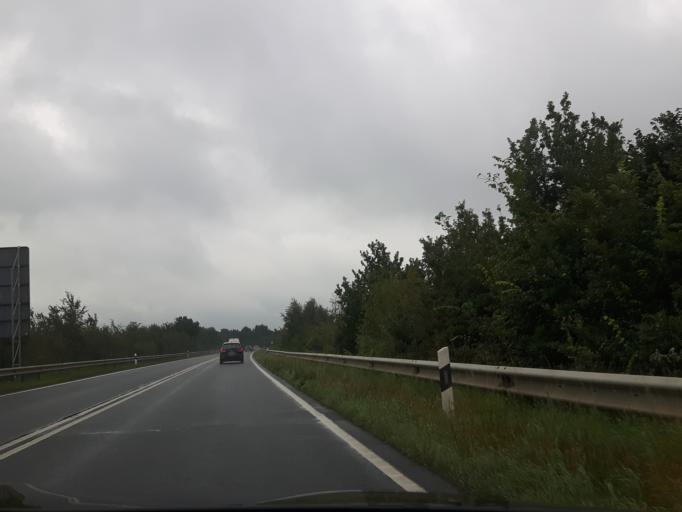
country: DE
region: Lower Saxony
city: Lingen
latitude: 52.5343
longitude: 7.3513
